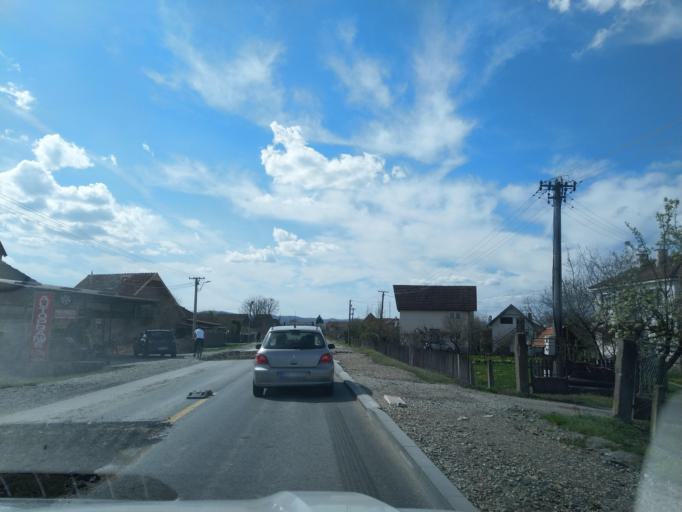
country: RS
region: Central Serbia
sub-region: Zlatiborski Okrug
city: Pozega
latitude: 43.8309
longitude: 20.0544
